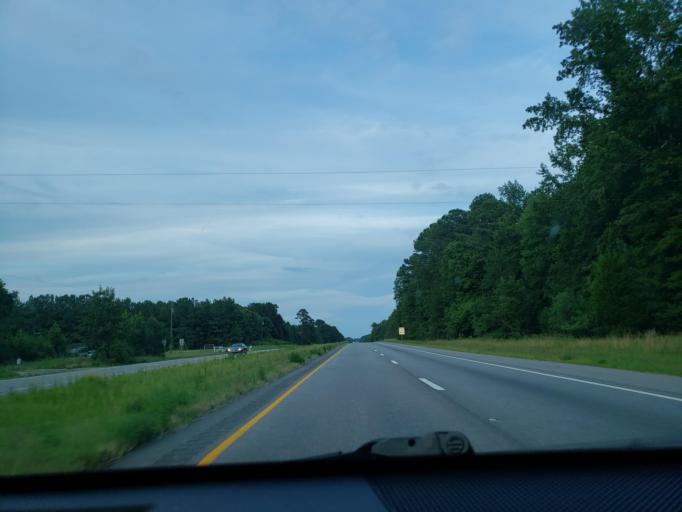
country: US
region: Virginia
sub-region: City of Emporia
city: Emporia
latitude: 36.6958
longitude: -77.3407
